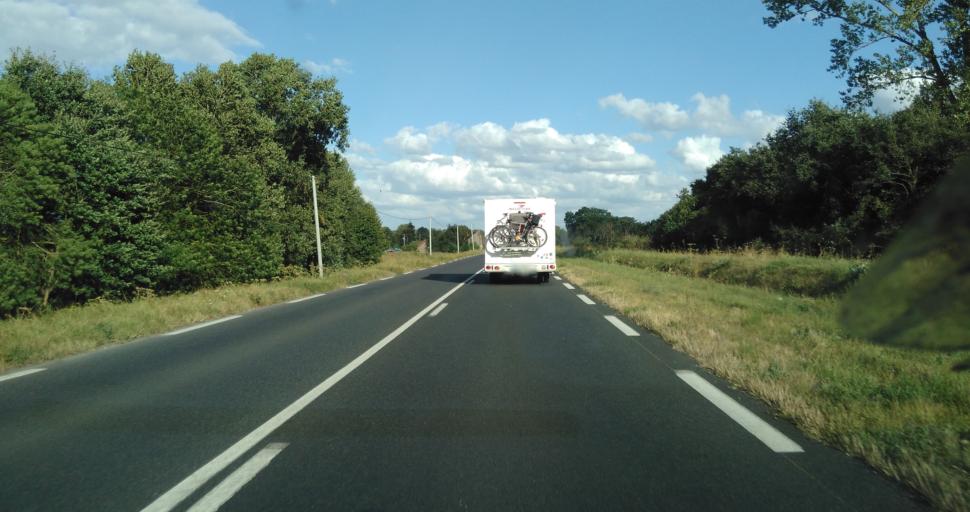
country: FR
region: Centre
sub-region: Departement d'Indre-et-Loire
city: Noizay
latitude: 47.4036
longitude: 0.9047
